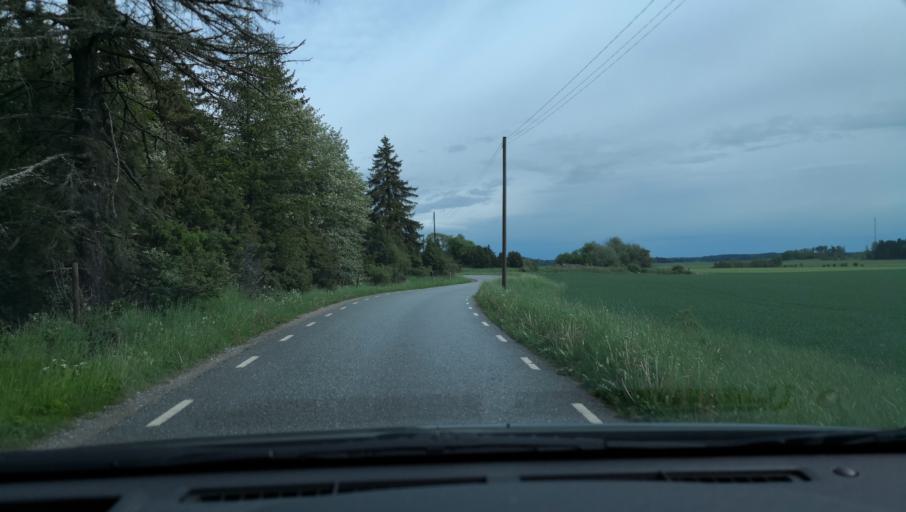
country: SE
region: Uppsala
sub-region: Enkopings Kommun
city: Orsundsbro
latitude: 59.7063
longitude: 17.3961
